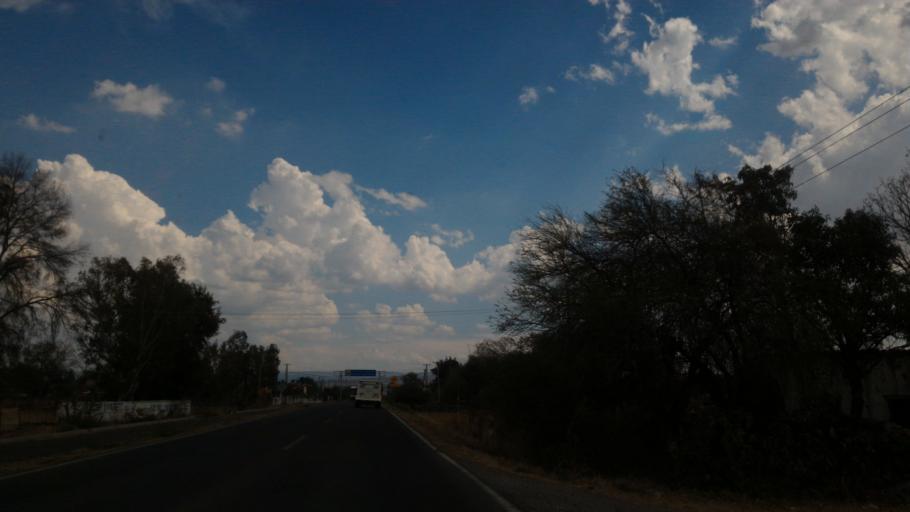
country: MX
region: Guanajuato
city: Ciudad Manuel Doblado
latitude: 20.7455
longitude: -101.9590
